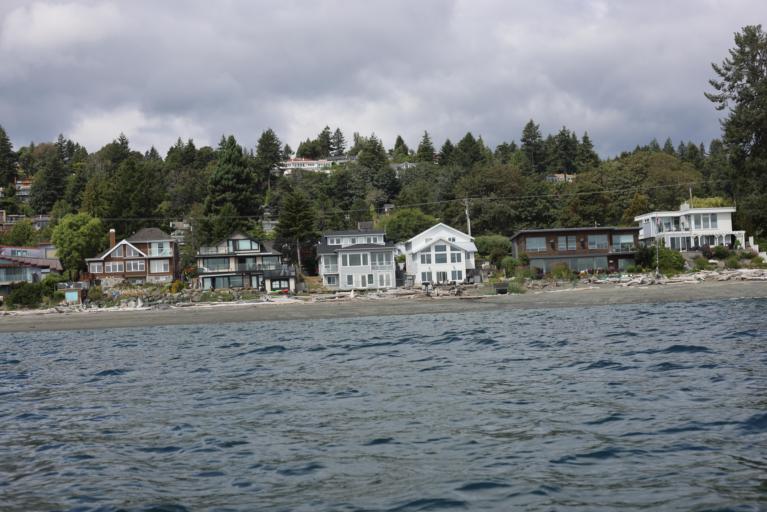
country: CA
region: British Columbia
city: Victoria
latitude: 48.5207
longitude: -123.3646
